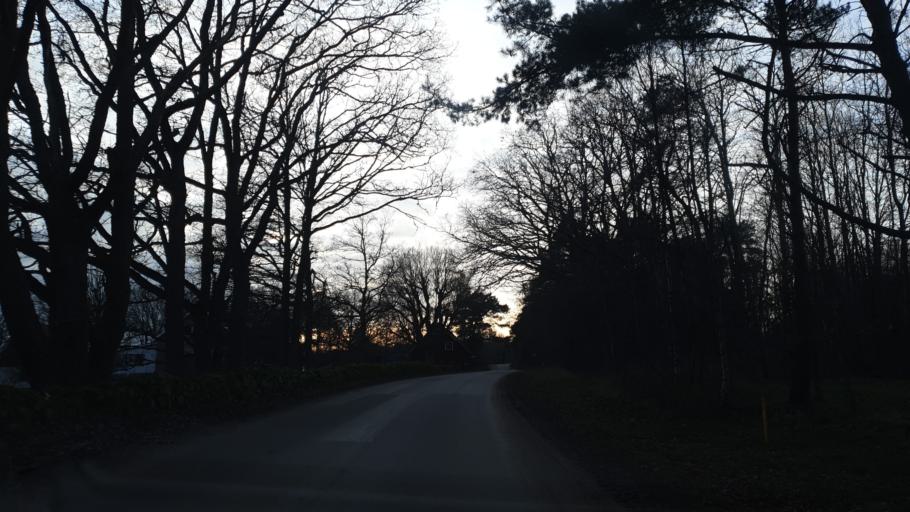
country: SE
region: Blekinge
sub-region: Karlskrona Kommun
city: Jaemjoe
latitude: 56.1592
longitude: 15.9131
